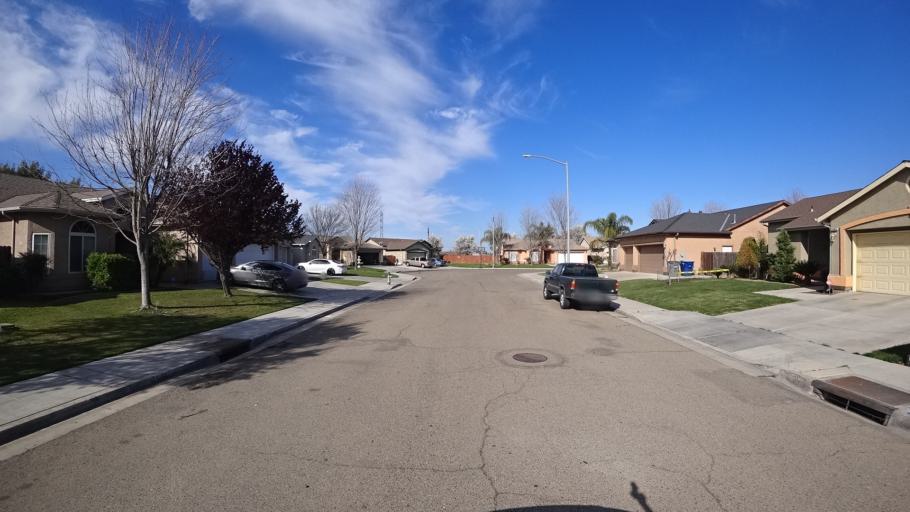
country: US
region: California
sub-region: Fresno County
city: West Park
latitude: 36.8013
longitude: -119.8972
